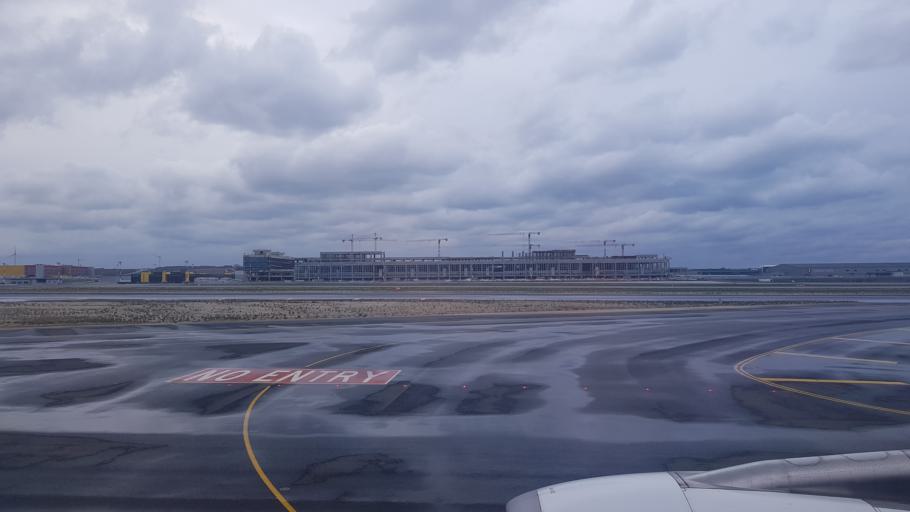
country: TR
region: Istanbul
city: Durusu
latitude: 41.2772
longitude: 28.7296
